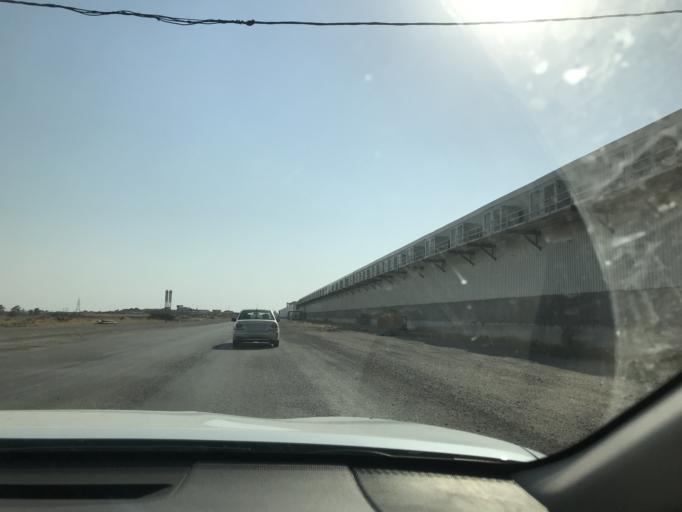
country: IQ
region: Arbil
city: Erbil
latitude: 36.1686
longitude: 43.9175
